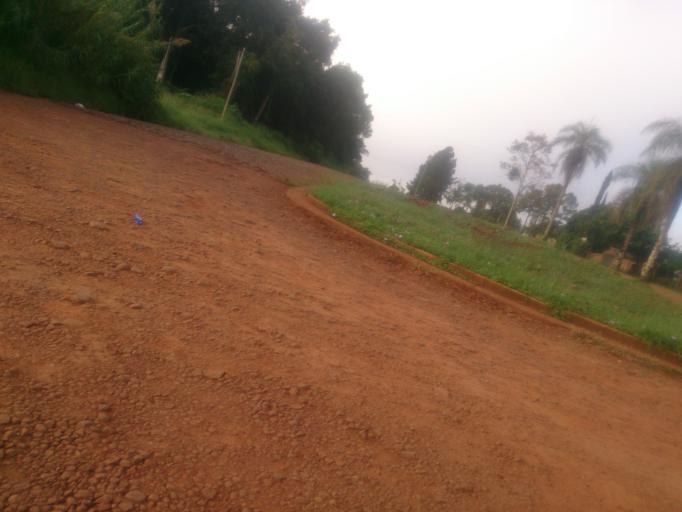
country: AR
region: Misiones
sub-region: Departamento de Obera
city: Obera
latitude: -27.4716
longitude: -55.1063
